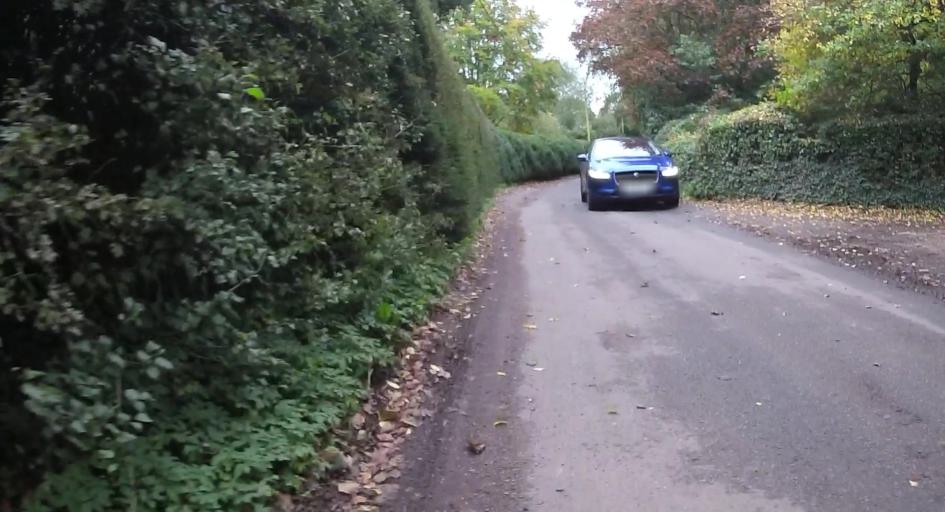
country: GB
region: England
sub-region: Hampshire
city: Four Marks
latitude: 51.1463
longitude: -1.1038
